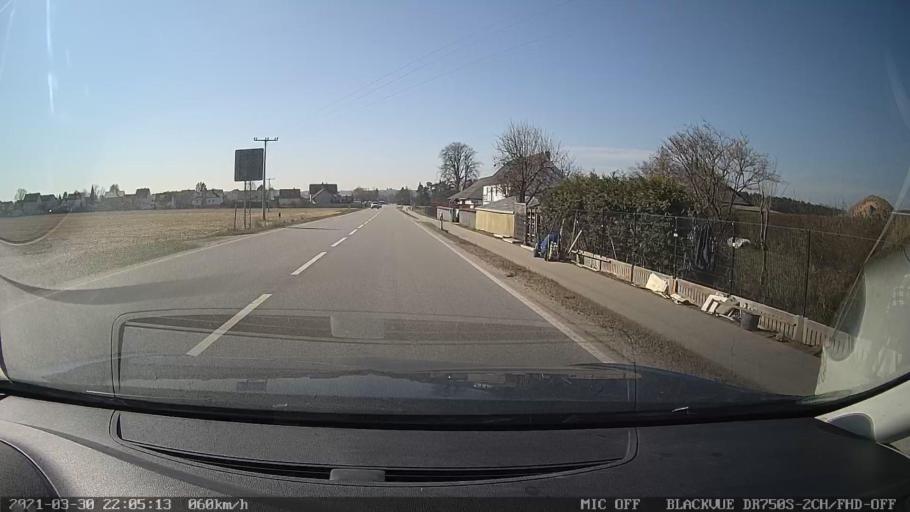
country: DE
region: Bavaria
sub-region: Upper Palatinate
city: Regenstauf
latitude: 49.0988
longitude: 12.1241
